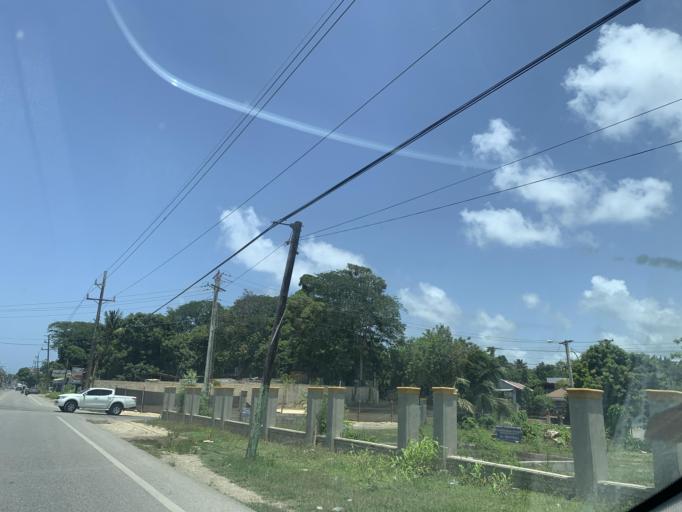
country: DO
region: Puerto Plata
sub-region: Puerto Plata
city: Puerto Plata
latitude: 19.7478
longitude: -70.5869
